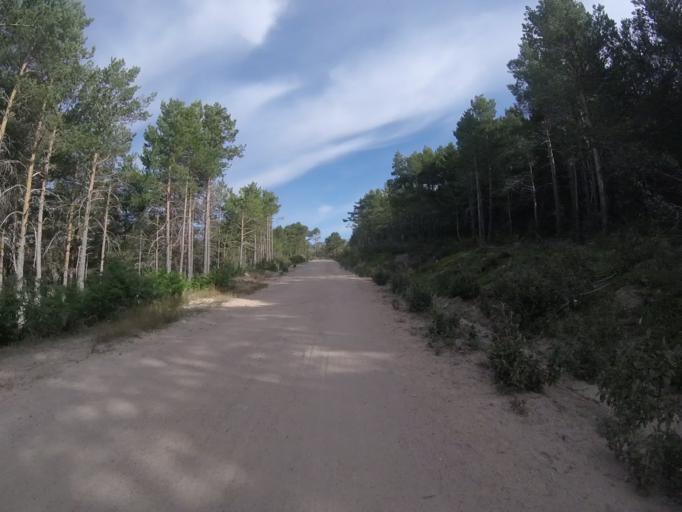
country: ES
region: Castille and Leon
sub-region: Provincia de Avila
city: Peguerinos
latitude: 40.6559
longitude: -4.1851
